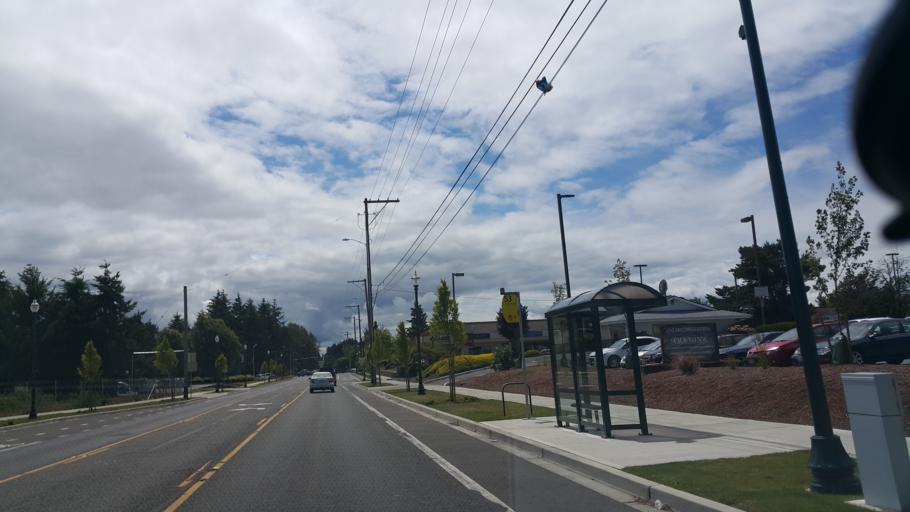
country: US
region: Washington
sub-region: Pierce County
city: Fircrest
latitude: 47.2399
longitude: -122.5264
